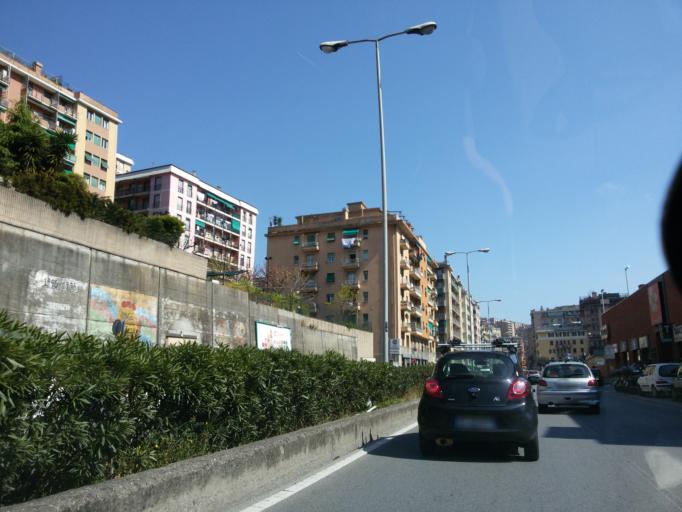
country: IT
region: Liguria
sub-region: Provincia di Genova
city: Genoa
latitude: 44.4195
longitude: 8.9508
